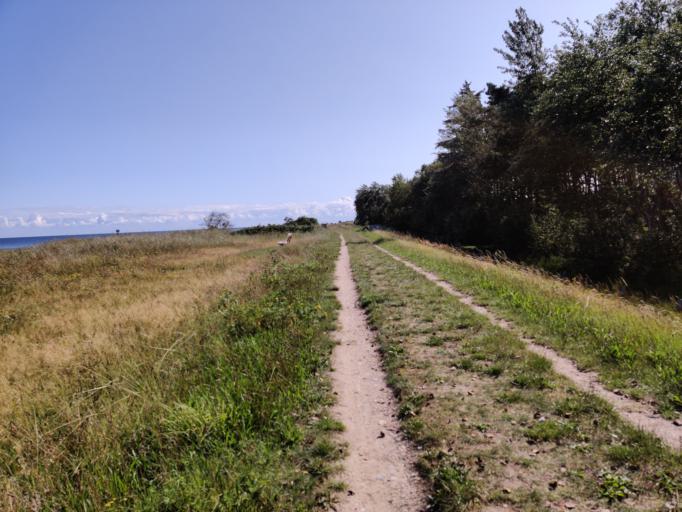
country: DK
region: Zealand
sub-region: Guldborgsund Kommune
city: Nykobing Falster
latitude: 54.5915
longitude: 11.9700
